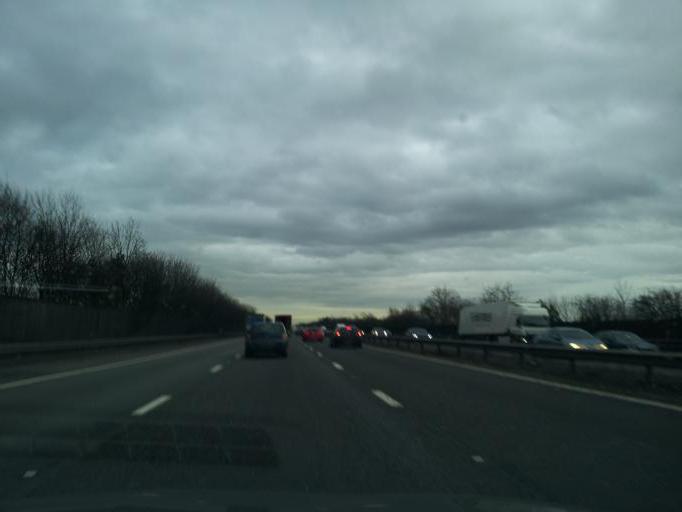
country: GB
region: England
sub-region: Warwickshire
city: Exhall
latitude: 52.4532
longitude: -1.4721
